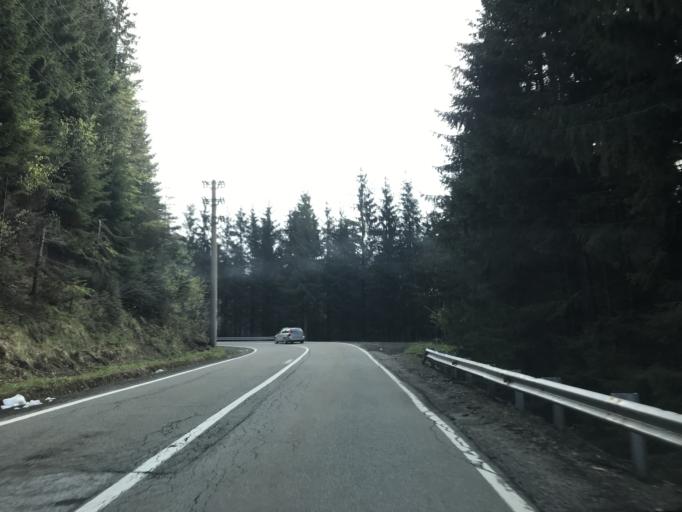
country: RO
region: Sibiu
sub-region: Comuna Cartisoara
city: Cartisoara
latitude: 45.6508
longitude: 24.6050
